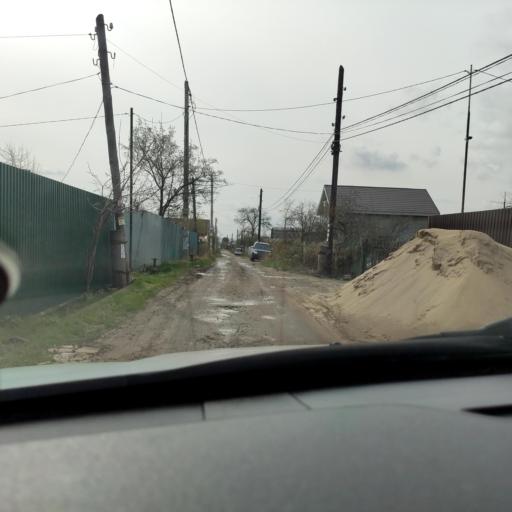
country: RU
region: Samara
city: Petra-Dubrava
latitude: 53.2855
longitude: 50.2963
